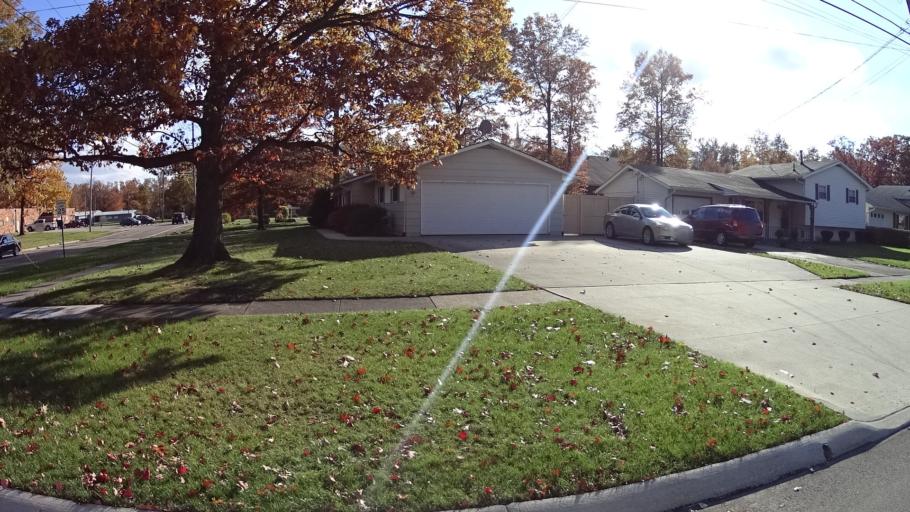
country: US
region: Ohio
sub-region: Lorain County
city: Sheffield
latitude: 41.4324
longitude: -82.1271
